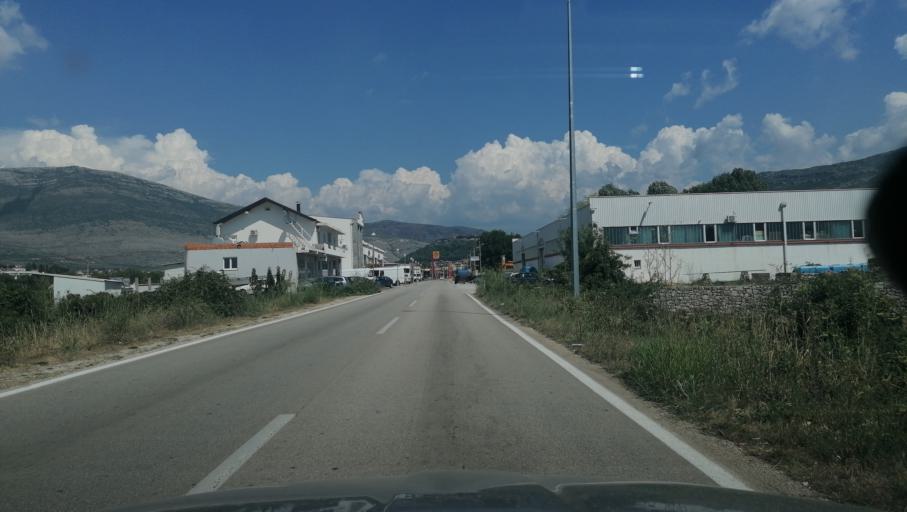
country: BA
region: Republika Srpska
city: Trebinje
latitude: 42.7040
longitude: 18.3331
